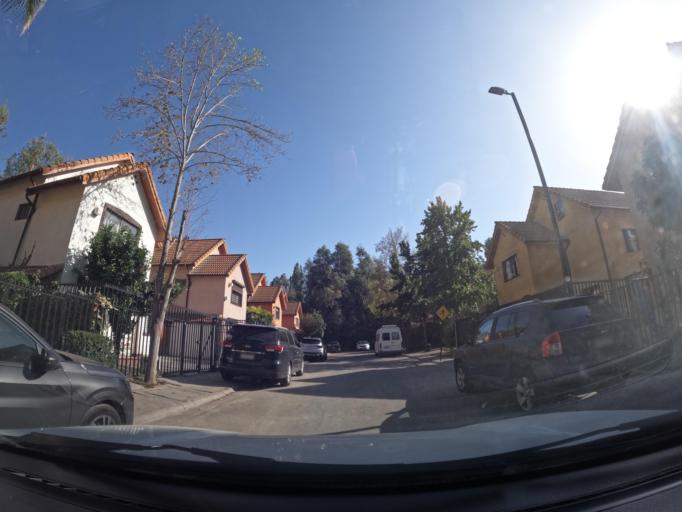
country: CL
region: Santiago Metropolitan
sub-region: Provincia de Santiago
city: Villa Presidente Frei, Nunoa, Santiago, Chile
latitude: -33.5105
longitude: -70.5495
